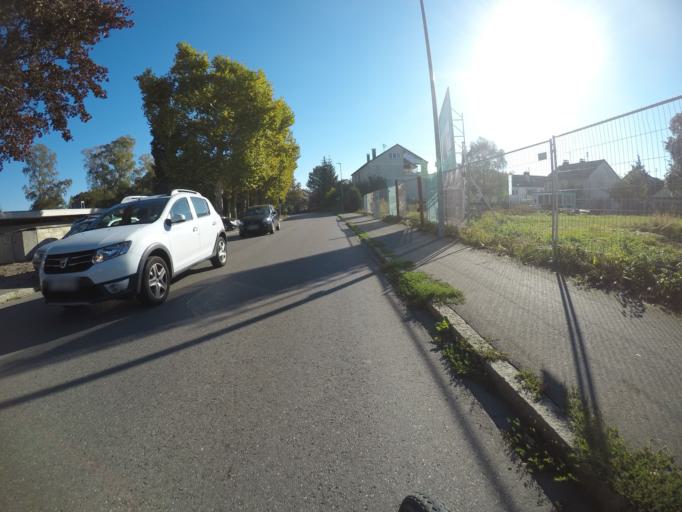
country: DE
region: Baden-Wuerttemberg
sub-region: Regierungsbezirk Stuttgart
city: Leinfelden-Echterdingen
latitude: 48.6906
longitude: 9.1710
